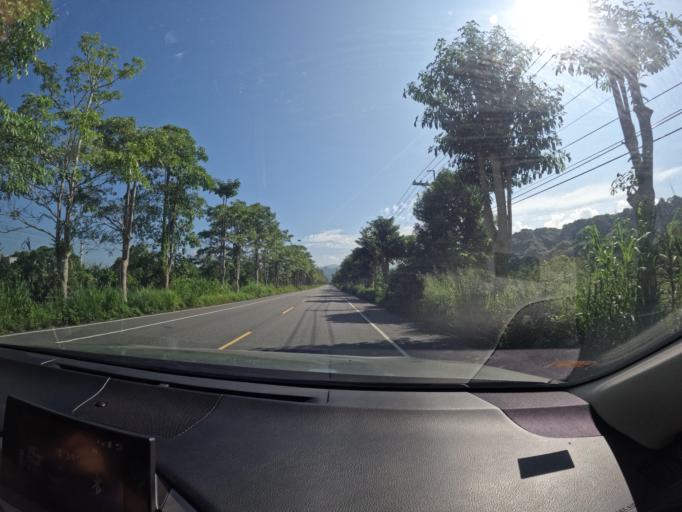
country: TW
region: Taiwan
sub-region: Hualien
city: Hualian
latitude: 23.4810
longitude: 121.3645
